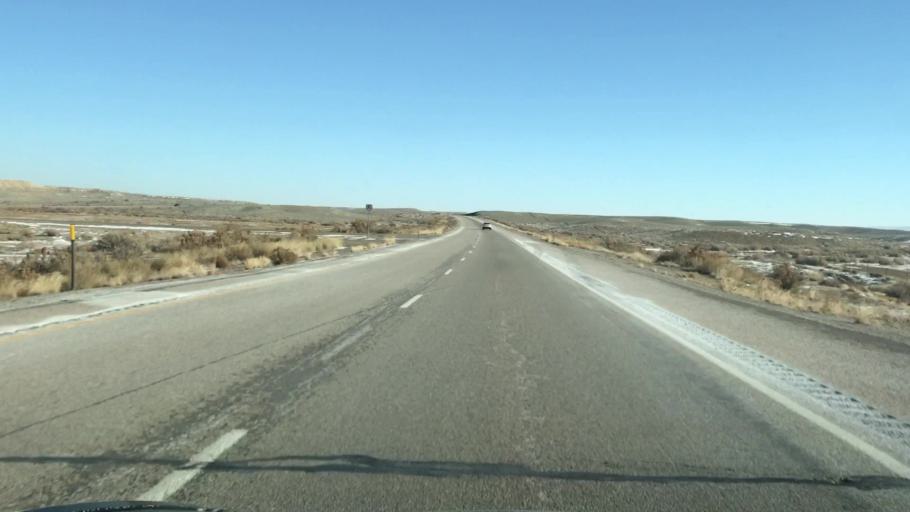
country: US
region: Utah
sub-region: Grand County
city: Moab
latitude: 38.9754
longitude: -109.3514
